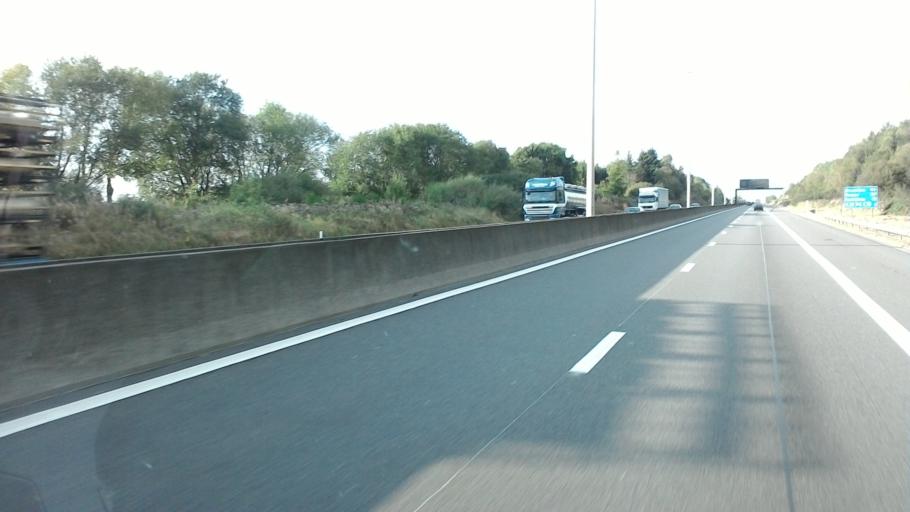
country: BE
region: Wallonia
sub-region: Province du Luxembourg
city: Leglise
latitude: 49.8169
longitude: 5.5153
